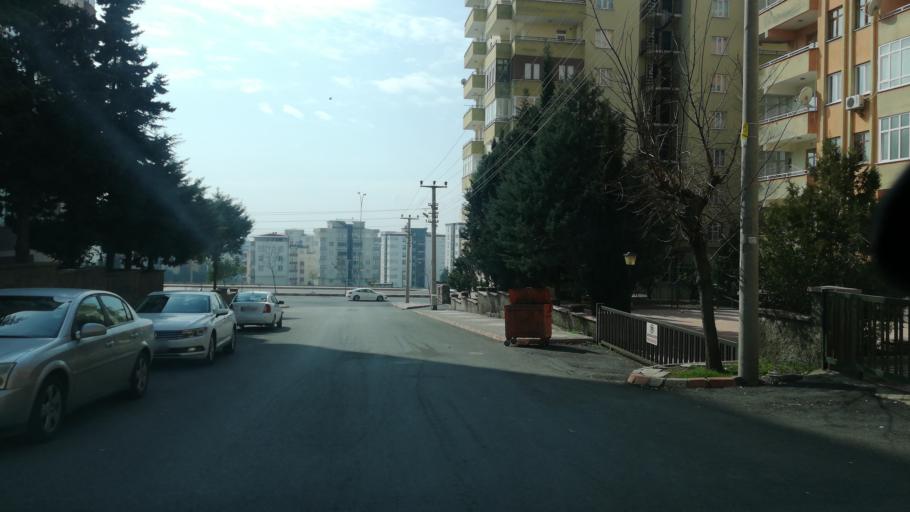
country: TR
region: Kahramanmaras
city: Kahramanmaras
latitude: 37.5874
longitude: 36.8836
